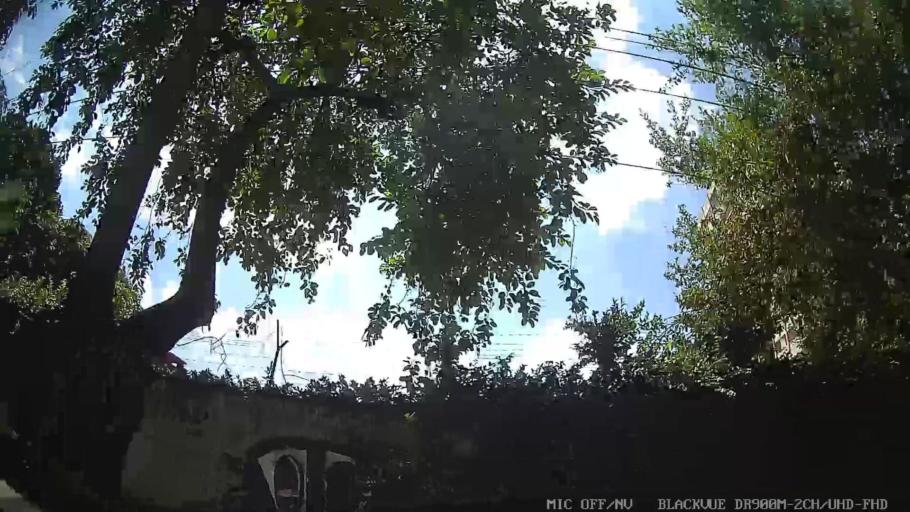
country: BR
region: Sao Paulo
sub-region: Taboao Da Serra
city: Taboao da Serra
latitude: -23.6502
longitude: -46.7564
